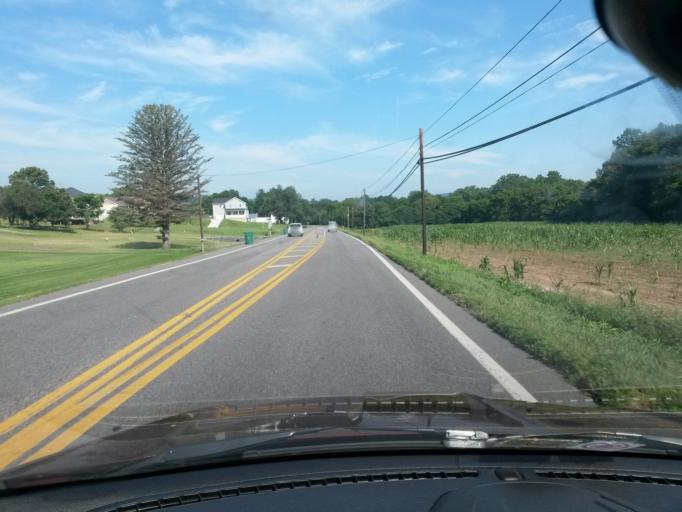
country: US
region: Virginia
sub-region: Rockingham County
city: Broadway
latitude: 38.6215
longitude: -78.8076
